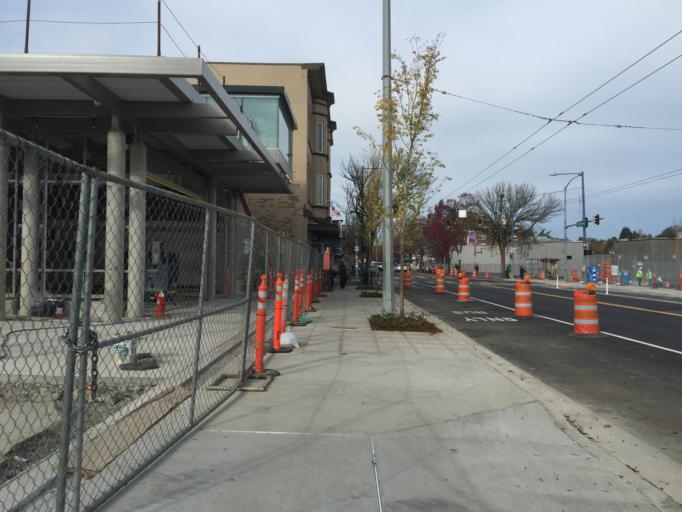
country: US
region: Washington
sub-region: King County
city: Seattle
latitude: 47.6181
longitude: -122.3210
